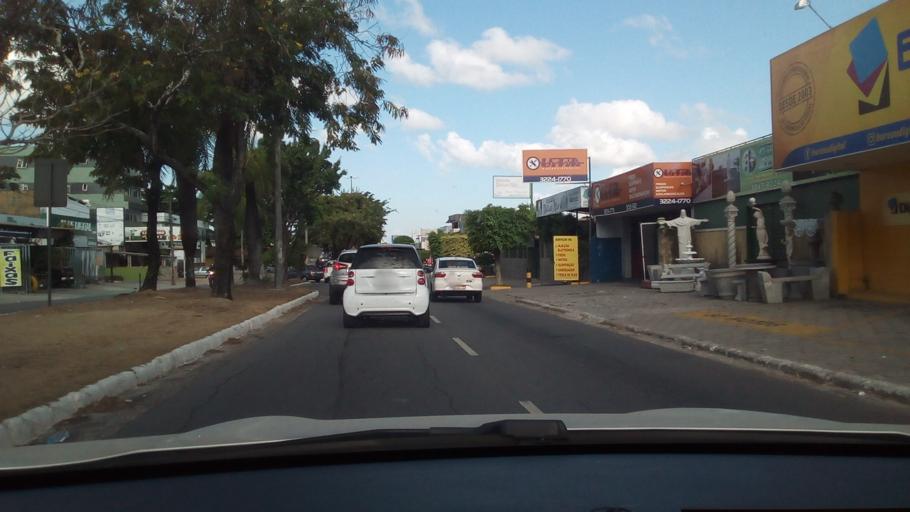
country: BR
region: Paraiba
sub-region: Joao Pessoa
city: Joao Pessoa
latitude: -7.1288
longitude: -34.8587
